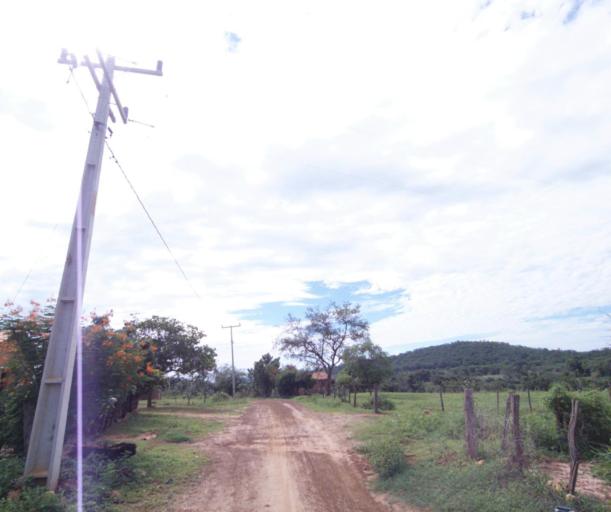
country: BR
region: Bahia
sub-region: Carinhanha
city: Carinhanha
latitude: -14.2370
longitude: -44.4020
